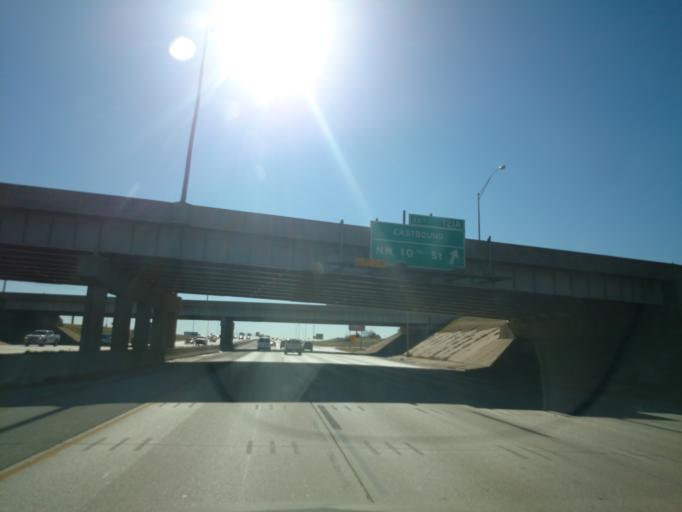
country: US
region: Oklahoma
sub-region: Oklahoma County
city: Warr Acres
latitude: 35.4790
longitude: -97.5788
